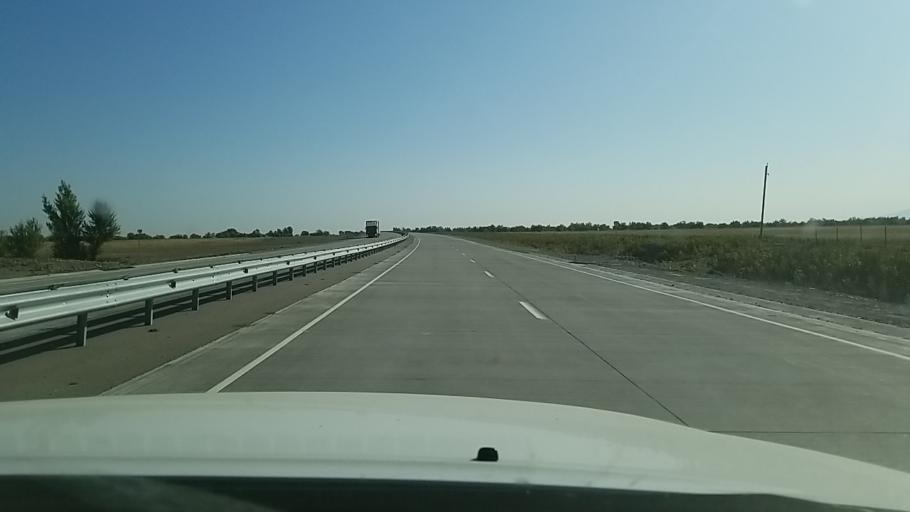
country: KZ
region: Almaty Oblysy
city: Turgen'
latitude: 43.5427
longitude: 77.7450
